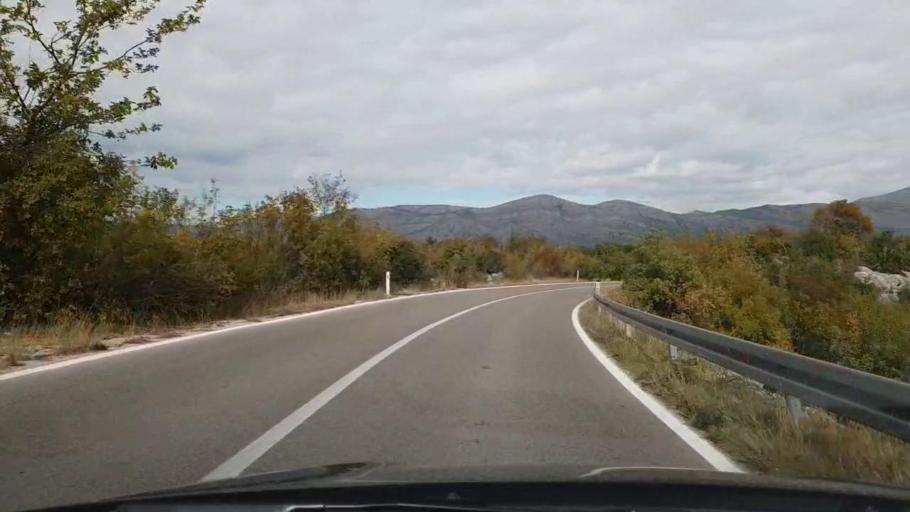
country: HR
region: Dubrovacko-Neretvanska
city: Jasenice
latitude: 42.6852
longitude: 18.2479
